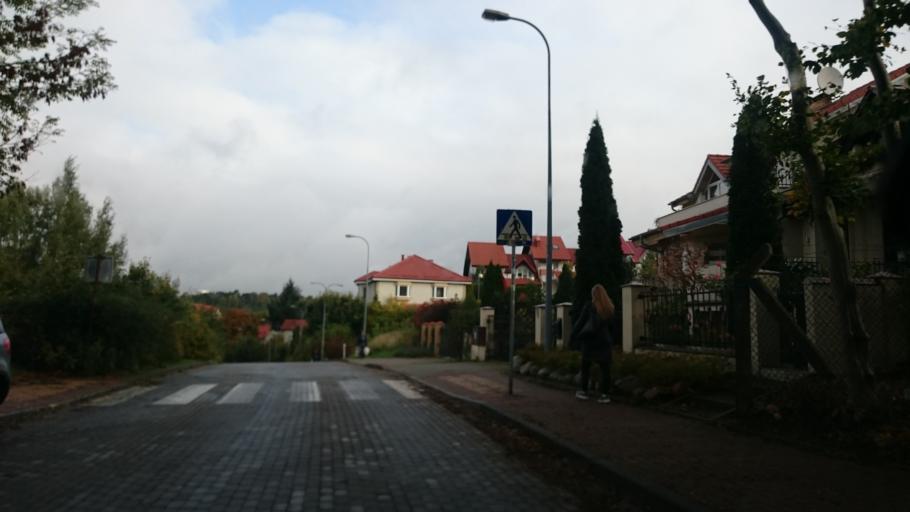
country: PL
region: Pomeranian Voivodeship
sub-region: Gdynia
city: Wielki Kack
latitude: 54.4650
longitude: 18.4937
